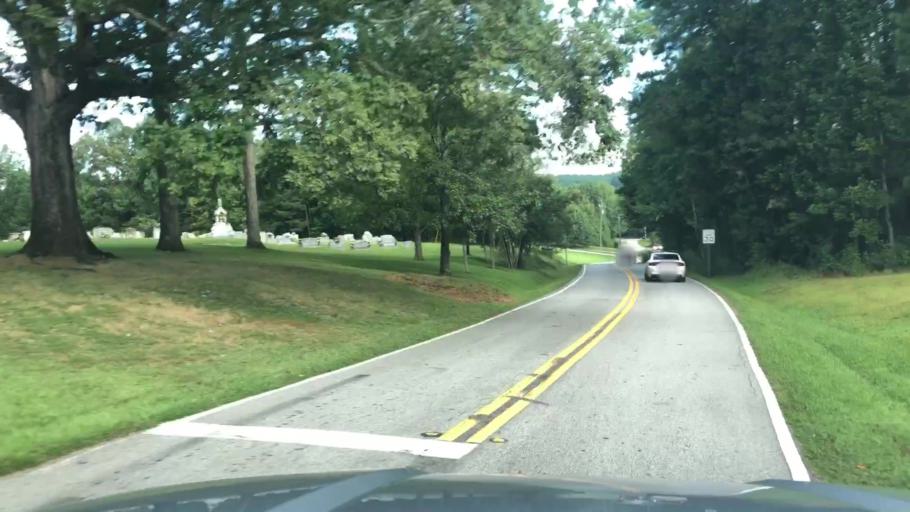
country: US
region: Georgia
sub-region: Paulding County
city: Dallas
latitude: 34.0318
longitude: -84.8606
